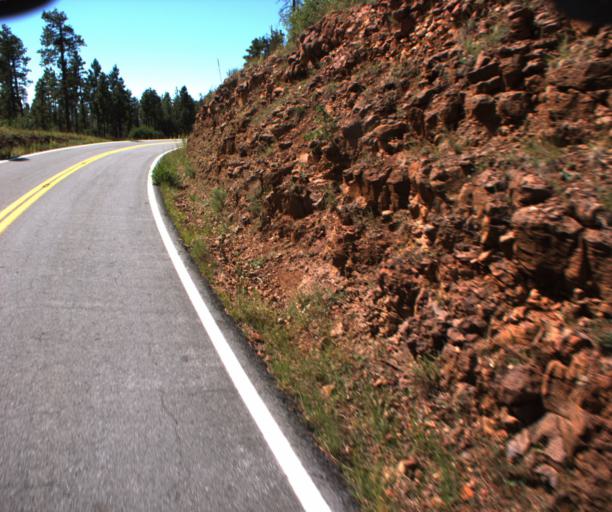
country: US
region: Arizona
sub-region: Apache County
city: Eagar
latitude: 33.7238
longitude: -109.1981
